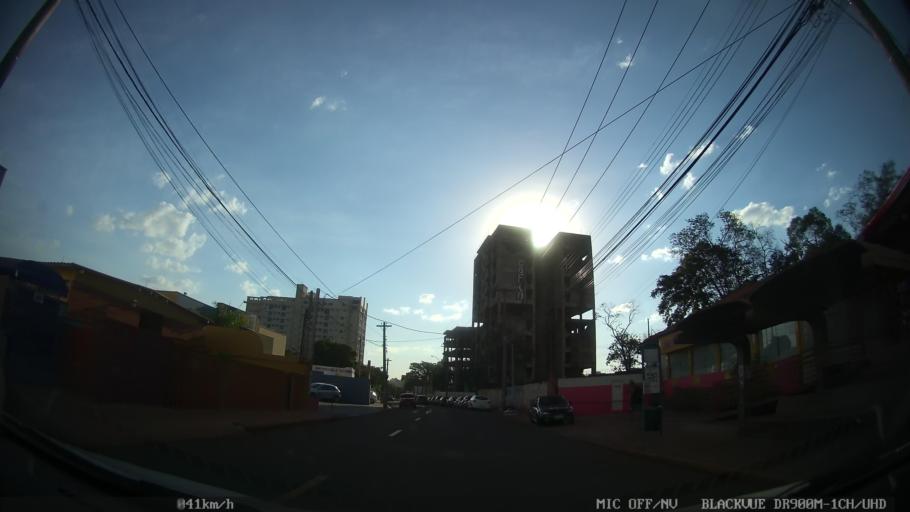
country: BR
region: Sao Paulo
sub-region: Ribeirao Preto
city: Ribeirao Preto
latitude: -21.1914
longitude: -47.7869
